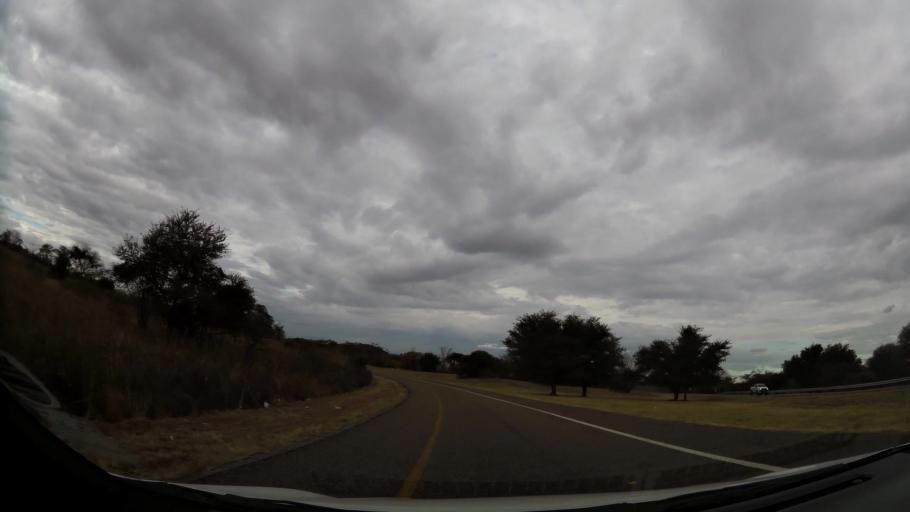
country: ZA
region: Limpopo
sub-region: Waterberg District Municipality
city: Modimolle
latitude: -24.6826
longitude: 28.5544
